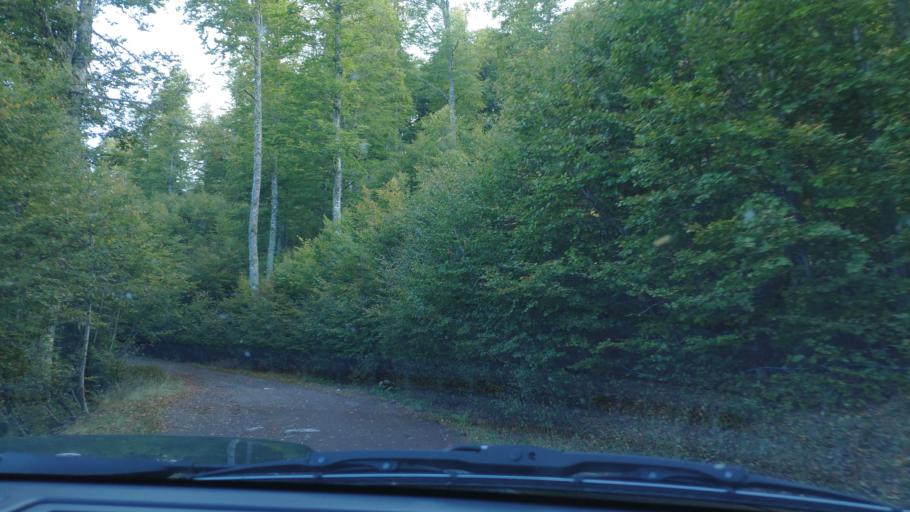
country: GR
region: West Macedonia
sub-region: Nomos Kastorias
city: Nestorio
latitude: 40.3151
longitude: 20.9107
